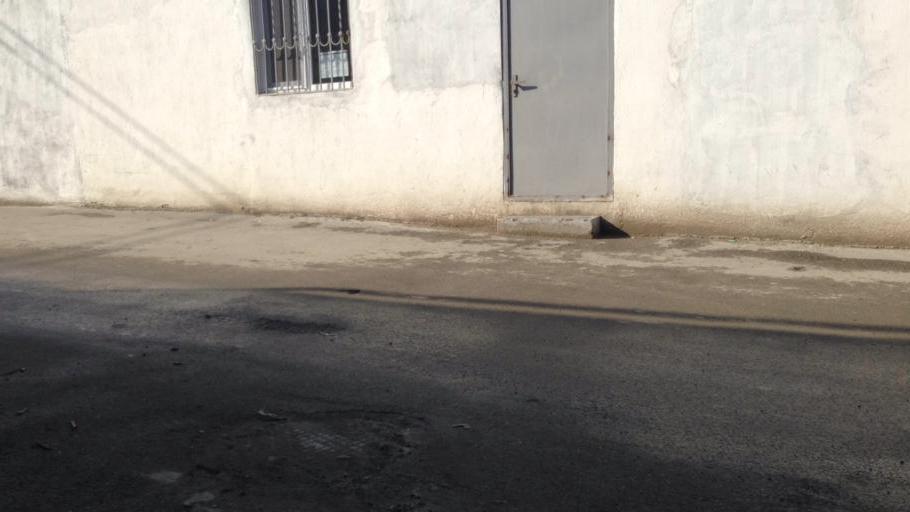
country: AZ
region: Baki
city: Binagadi
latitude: 40.4376
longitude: 49.8480
